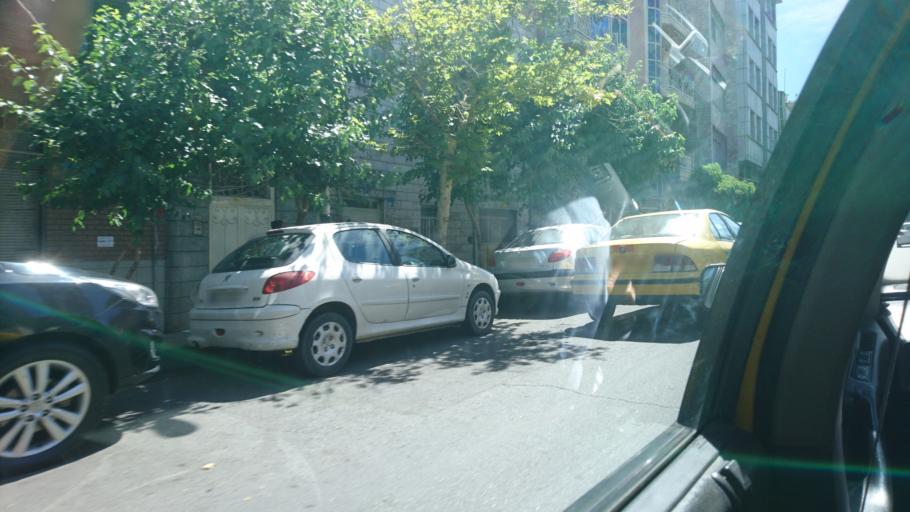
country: IR
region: Tehran
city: Tehran
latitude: 35.7015
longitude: 51.3912
